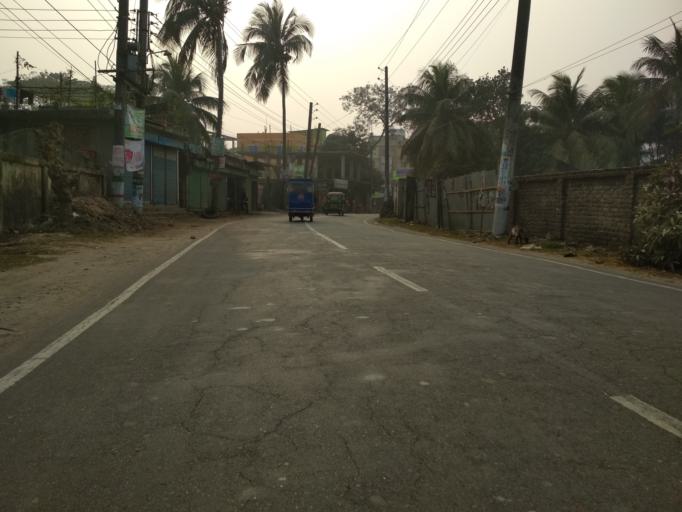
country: BD
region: Chittagong
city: Lakshmipur
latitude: 22.9367
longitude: 90.8406
